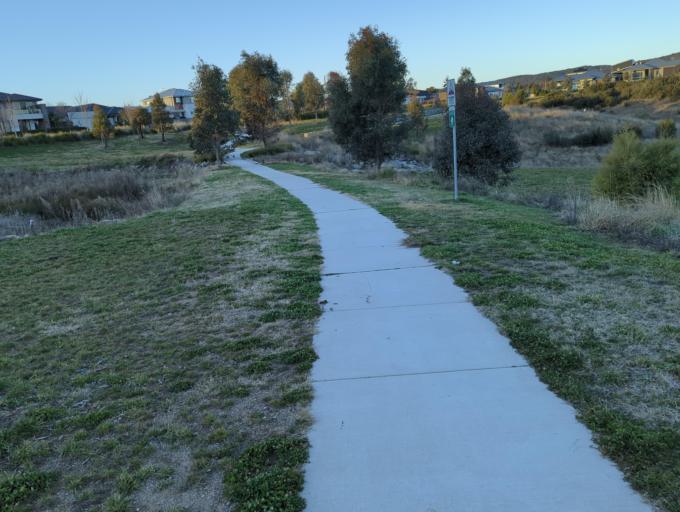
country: AU
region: New South Wales
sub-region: Queanbeyan
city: Queanbeyan
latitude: -35.4251
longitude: 149.2448
